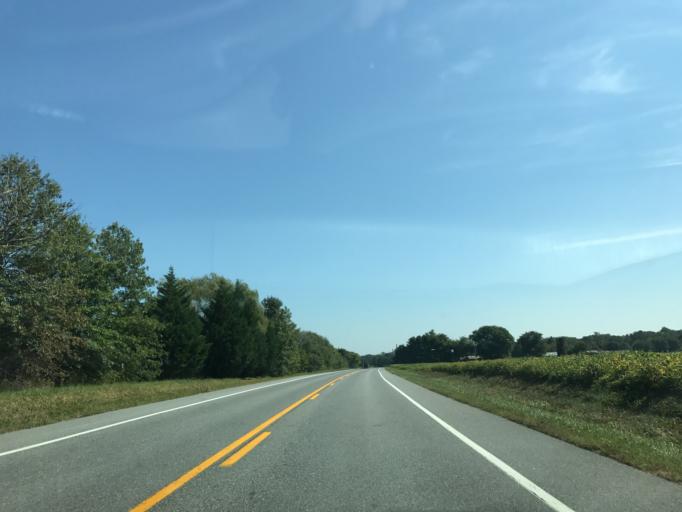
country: US
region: Delaware
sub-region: New Castle County
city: Townsend
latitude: 39.3017
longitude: -75.7642
